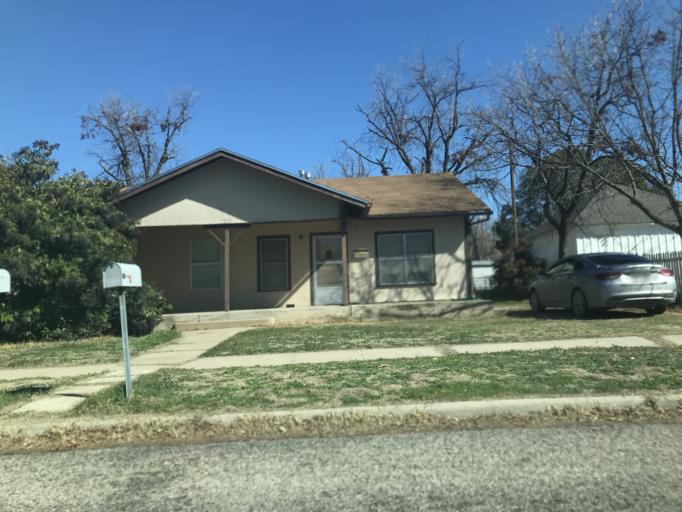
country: US
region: Texas
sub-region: Tom Green County
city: San Angelo
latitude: 31.4490
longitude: -100.4446
